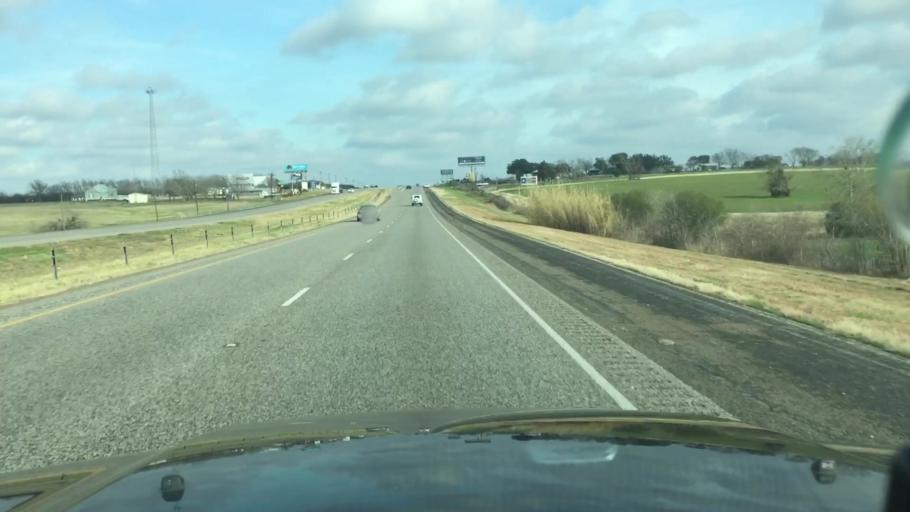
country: US
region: Texas
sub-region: Washington County
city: Brenham
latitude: 30.1398
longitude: -96.3030
